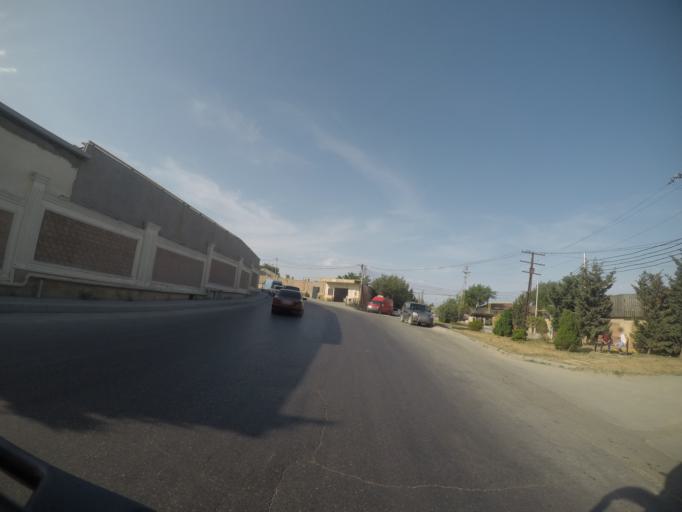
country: AZ
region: Baki
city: Binagadi
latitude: 40.4656
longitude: 49.8420
